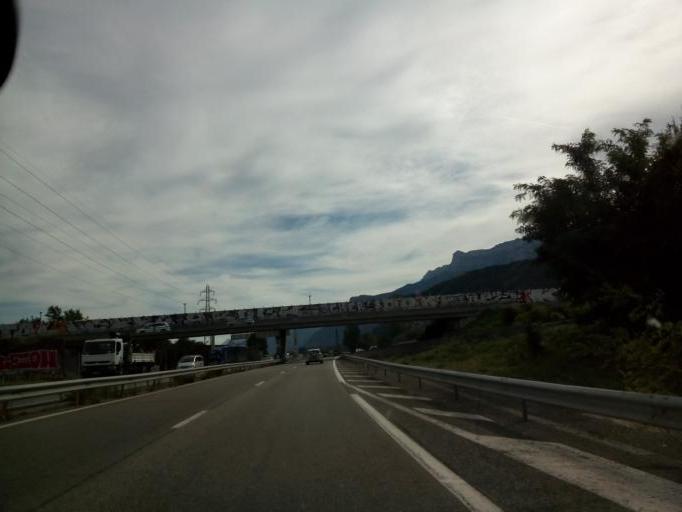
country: FR
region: Rhone-Alpes
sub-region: Departement de l'Isere
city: Grenoble
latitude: 45.1584
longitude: 5.7010
